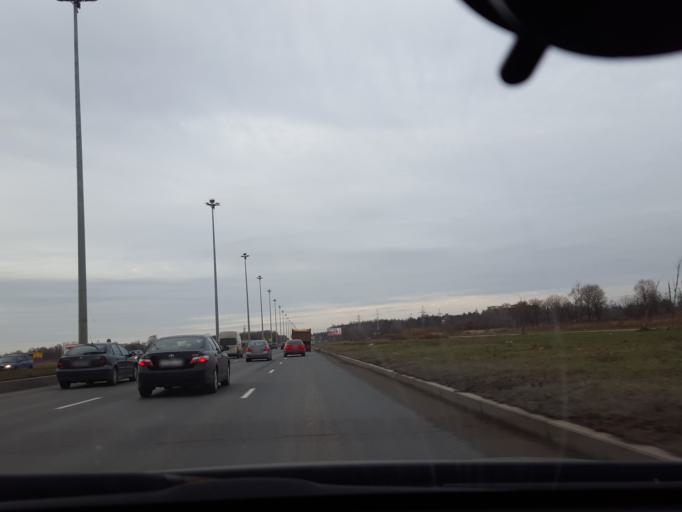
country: RU
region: Leningrad
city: Untolovo
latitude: 60.0391
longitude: 30.2430
